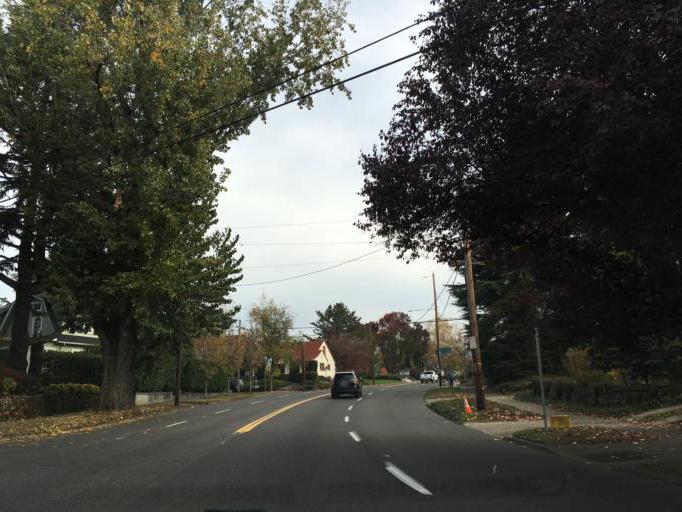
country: US
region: Oregon
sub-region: Multnomah County
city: Portland
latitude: 45.5229
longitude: -122.6181
